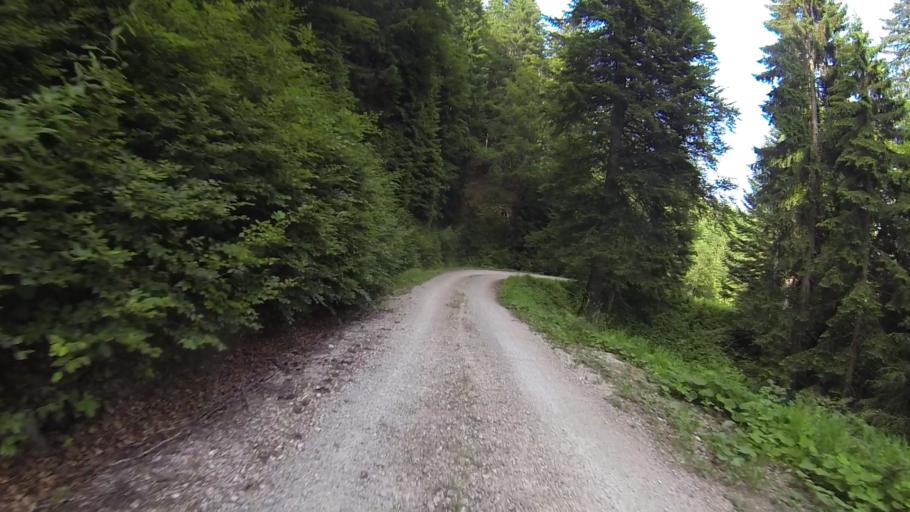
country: DE
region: Bavaria
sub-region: Swabia
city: Nesselwang
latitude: 47.5876
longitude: 10.5014
